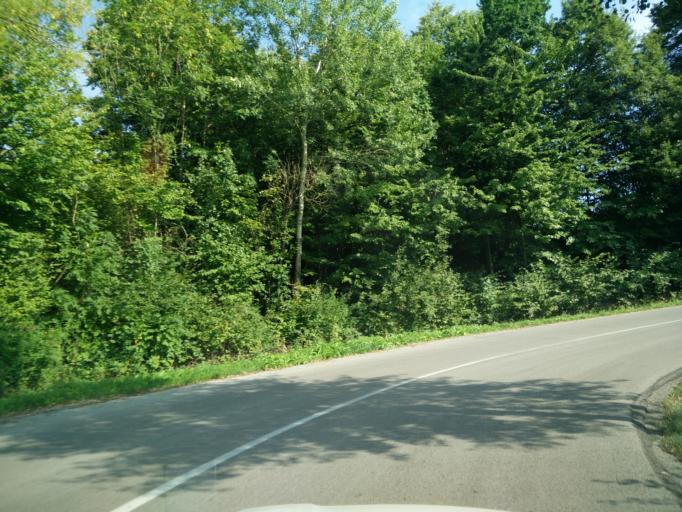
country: SK
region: Nitriansky
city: Prievidza
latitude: 48.6874
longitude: 18.6211
